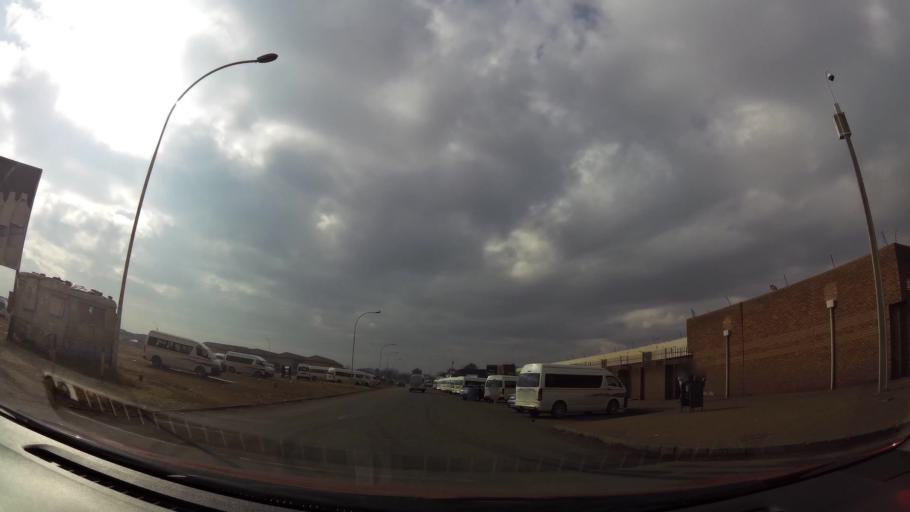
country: ZA
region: Gauteng
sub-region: Sedibeng District Municipality
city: Vanderbijlpark
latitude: -26.6955
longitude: 27.8375
